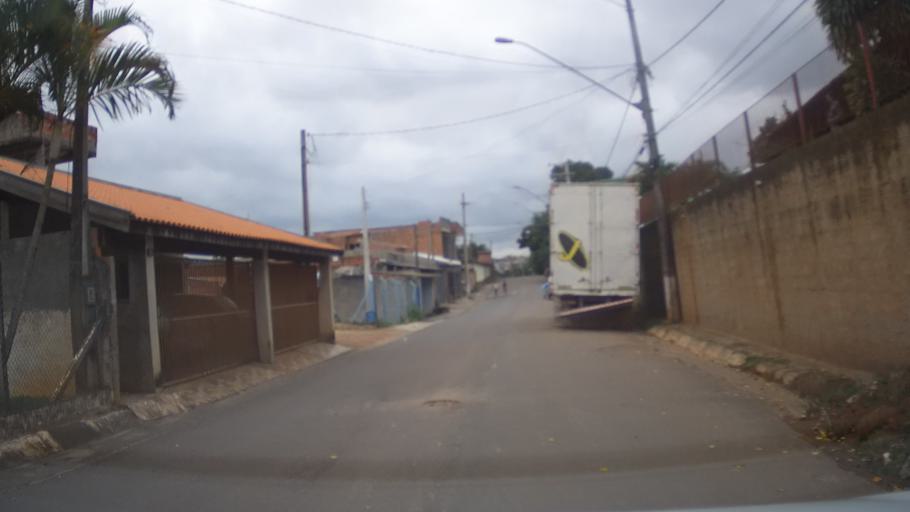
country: BR
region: Sao Paulo
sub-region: Louveira
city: Louveira
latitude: -23.0969
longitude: -46.9892
